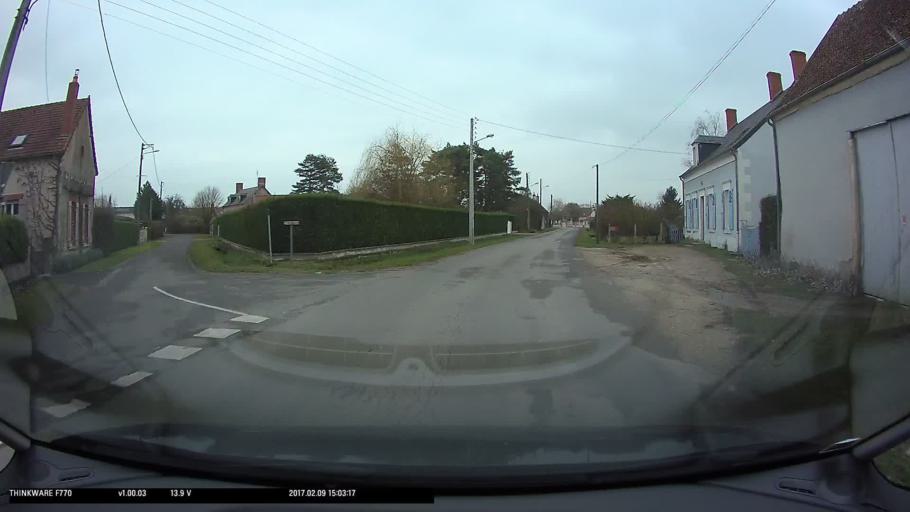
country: FR
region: Centre
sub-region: Departement du Cher
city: Orval
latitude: 46.8089
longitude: 2.4625
